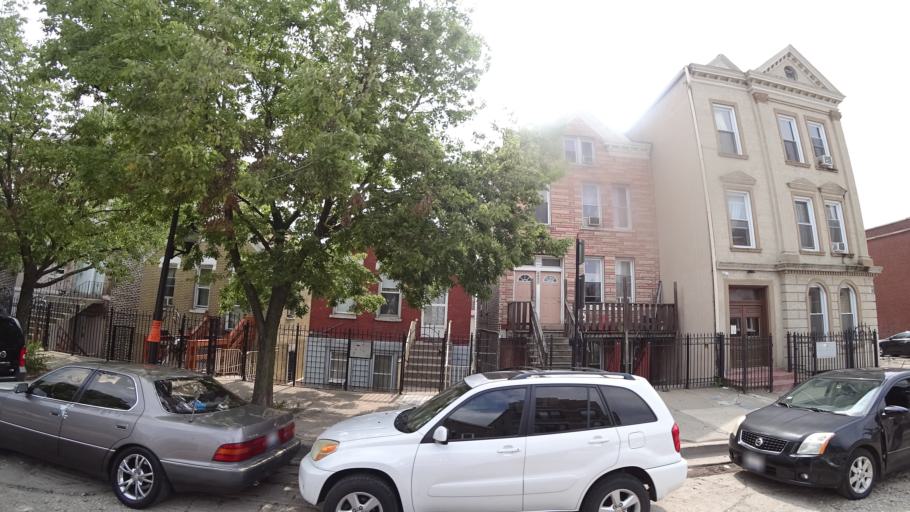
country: US
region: Illinois
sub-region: Cook County
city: Chicago
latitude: 41.8503
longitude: -87.6769
